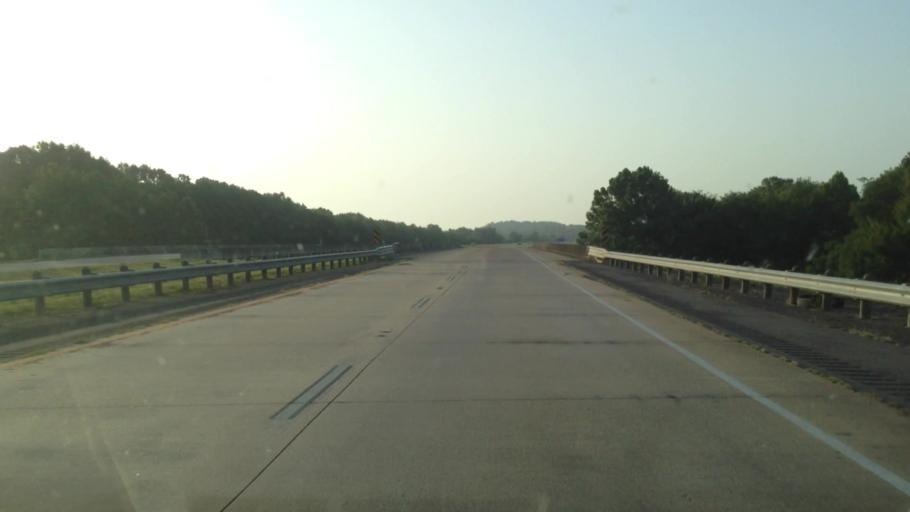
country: US
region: Louisiana
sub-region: Grant Parish
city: Colfax
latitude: 31.5025
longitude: -92.8755
